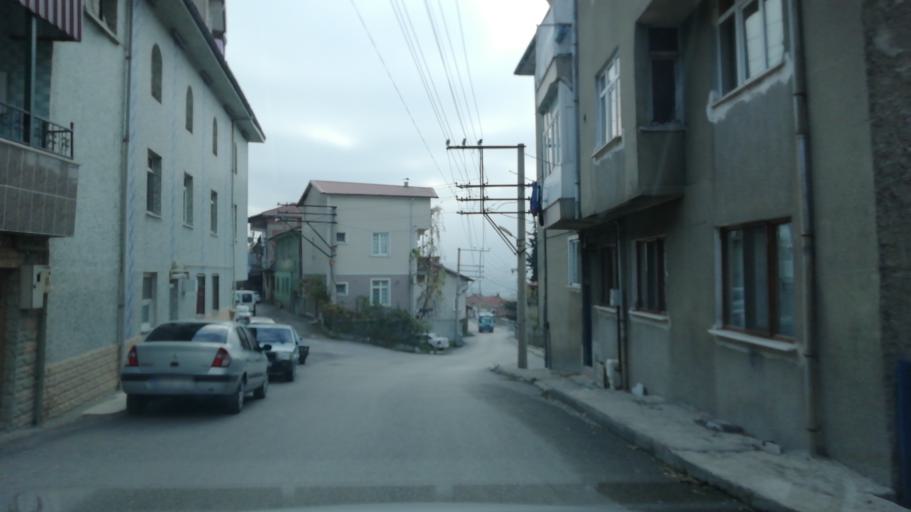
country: TR
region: Karabuk
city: Karabuk
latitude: 41.2158
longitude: 32.6287
